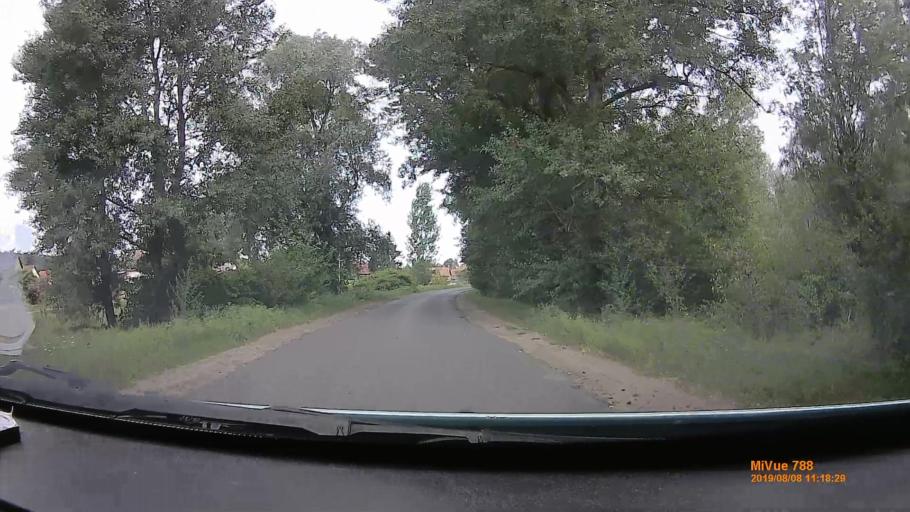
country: HU
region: Szabolcs-Szatmar-Bereg
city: Balkany
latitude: 47.7382
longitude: 21.8364
